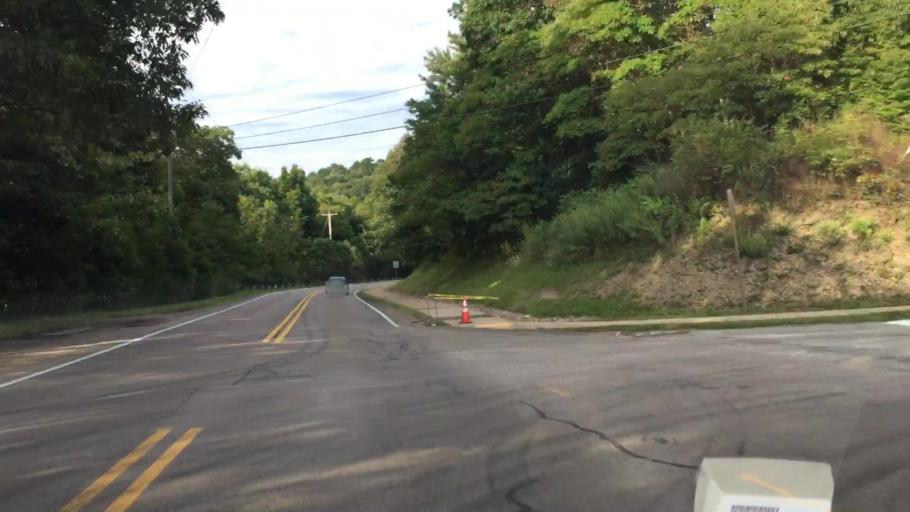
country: US
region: Pennsylvania
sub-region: Butler County
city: Fox Run
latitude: 40.7368
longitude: -80.1044
